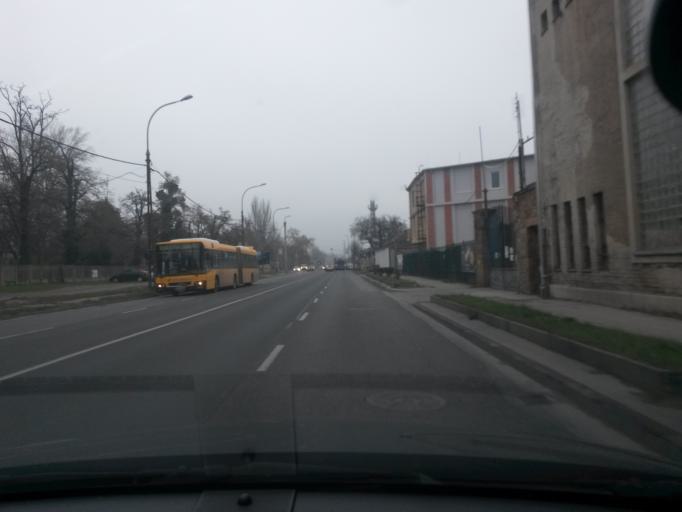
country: HU
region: Budapest
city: Budapest IV. keruelet
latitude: 47.5811
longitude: 19.0817
